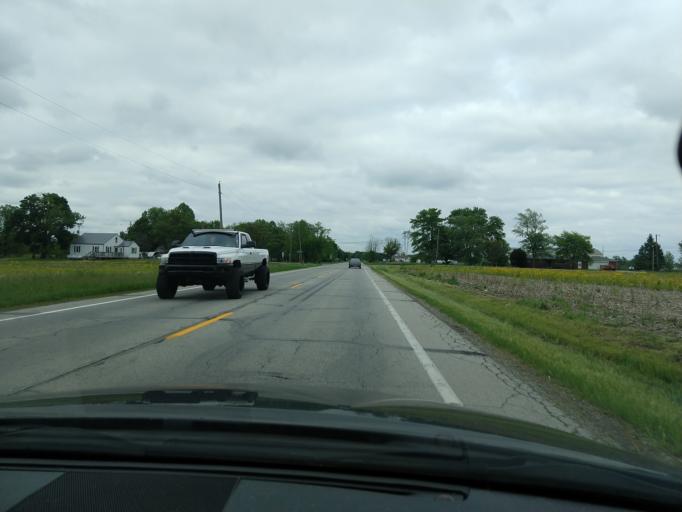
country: US
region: Indiana
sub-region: Madison County
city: Lapel
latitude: 40.0611
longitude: -85.8834
